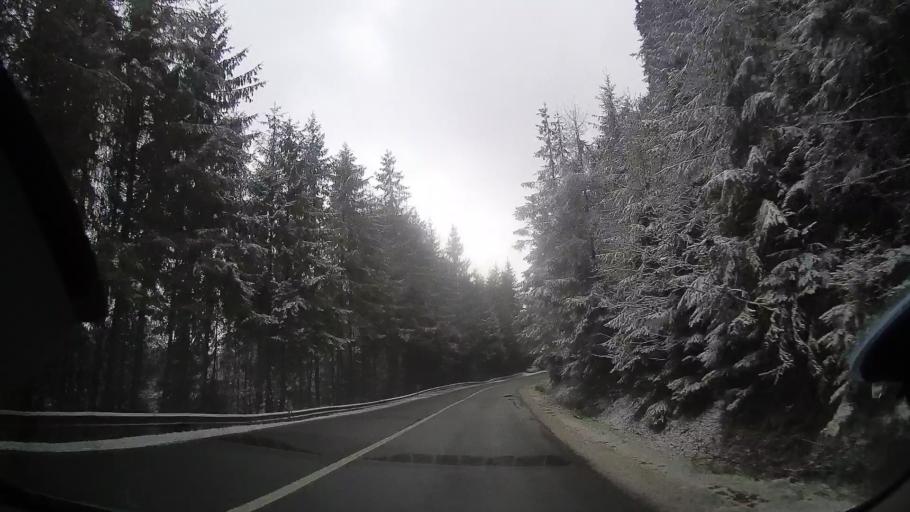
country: RO
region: Cluj
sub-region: Comuna Belis
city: Belis
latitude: 46.6594
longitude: 23.0563
